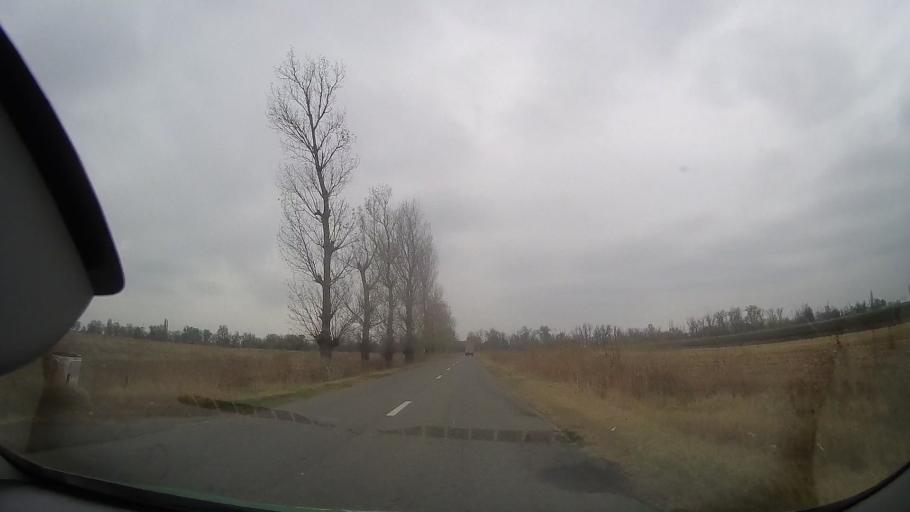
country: RO
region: Ialomita
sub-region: Comuna Garbovi
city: Garbovi
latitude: 44.7707
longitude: 26.7876
